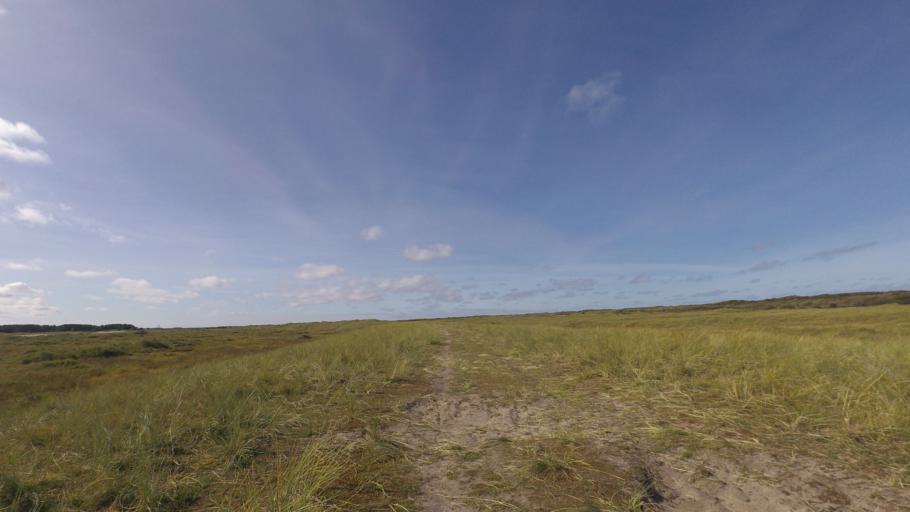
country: NL
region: Friesland
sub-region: Gemeente Ameland
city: Nes
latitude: 53.4544
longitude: 5.7088
